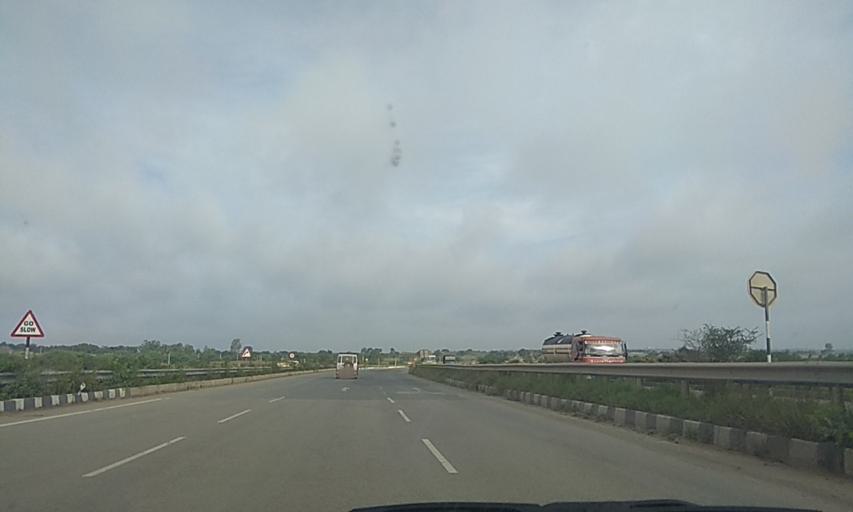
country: IN
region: Karnataka
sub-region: Haveri
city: Haveri
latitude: 14.7634
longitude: 75.4320
